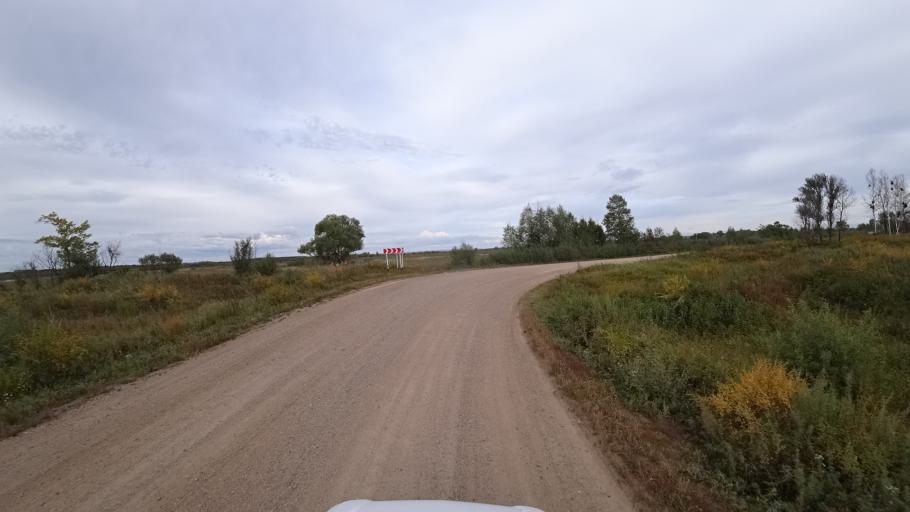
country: RU
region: Amur
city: Arkhara
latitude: 49.3785
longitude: 130.1766
